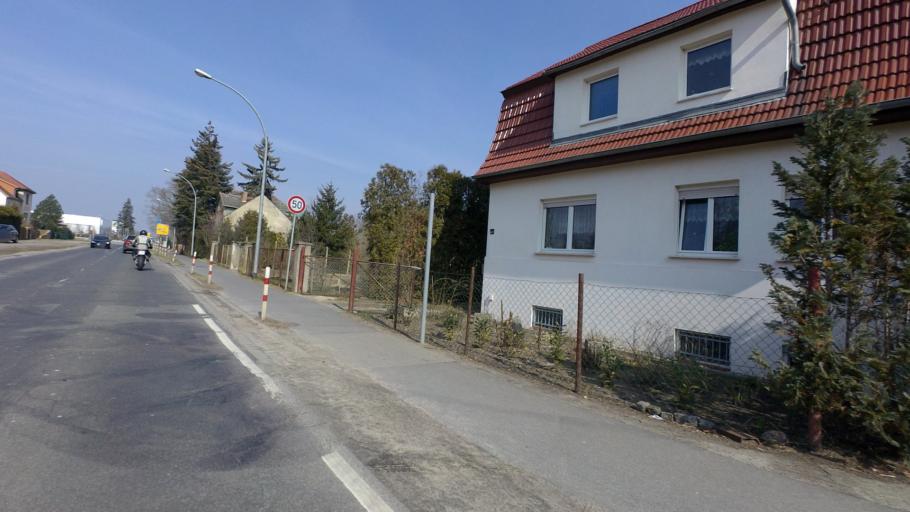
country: DE
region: Brandenburg
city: Werder
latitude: 52.3946
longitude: 12.9214
